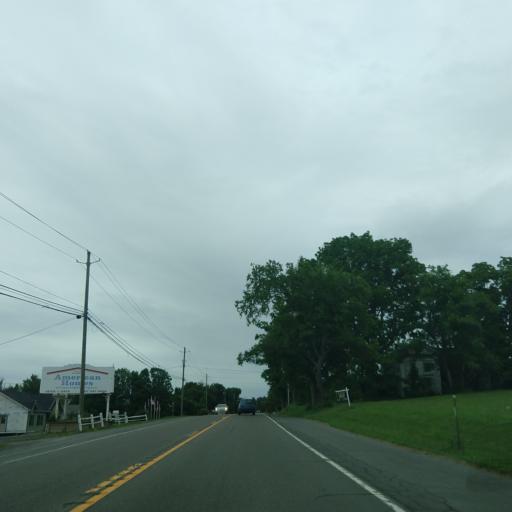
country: US
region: New York
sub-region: Tompkins County
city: Dryden
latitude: 42.4858
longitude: -76.3507
